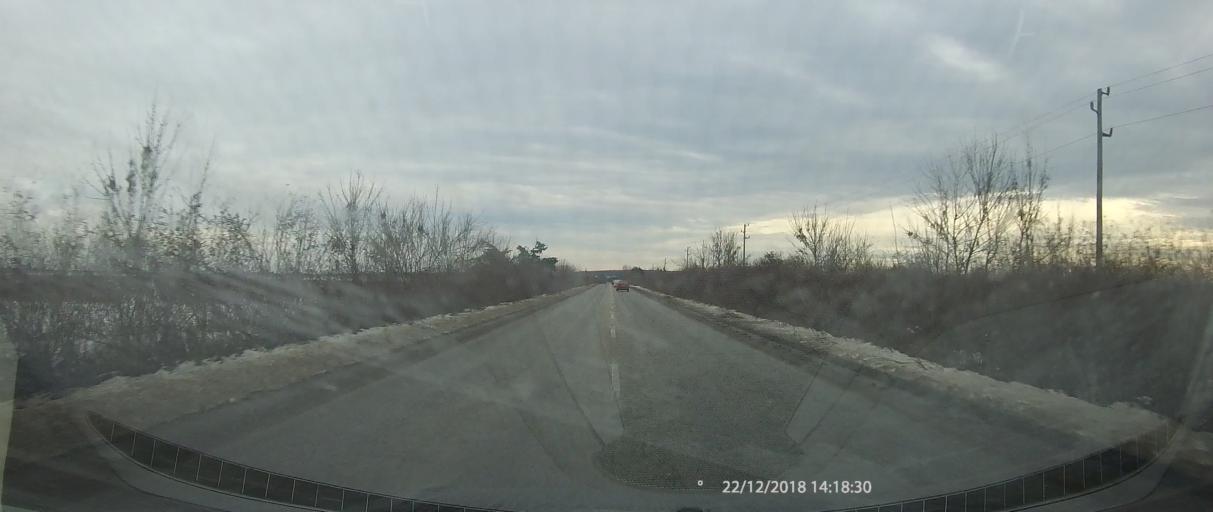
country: BG
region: Pleven
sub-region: Obshtina Pleven
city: Pleven
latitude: 43.4224
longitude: 24.7183
